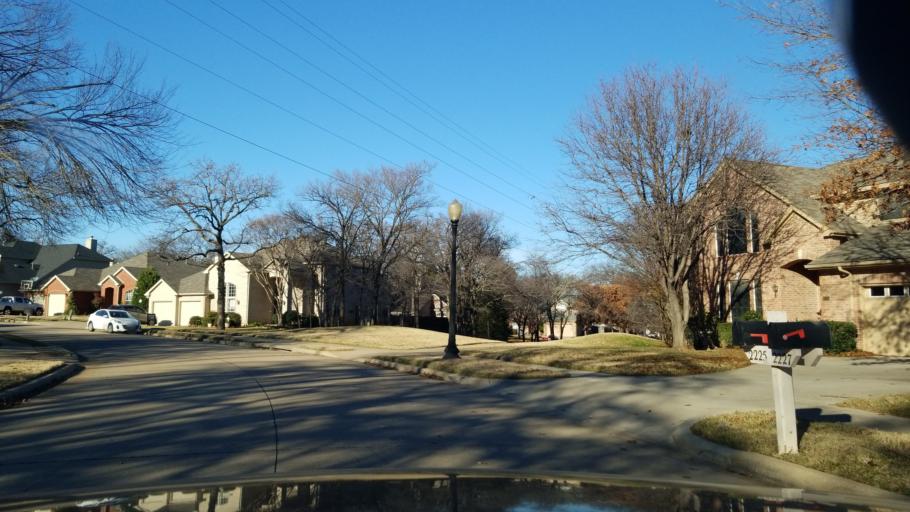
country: US
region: Texas
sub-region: Denton County
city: Corinth
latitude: 33.1572
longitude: -97.0741
